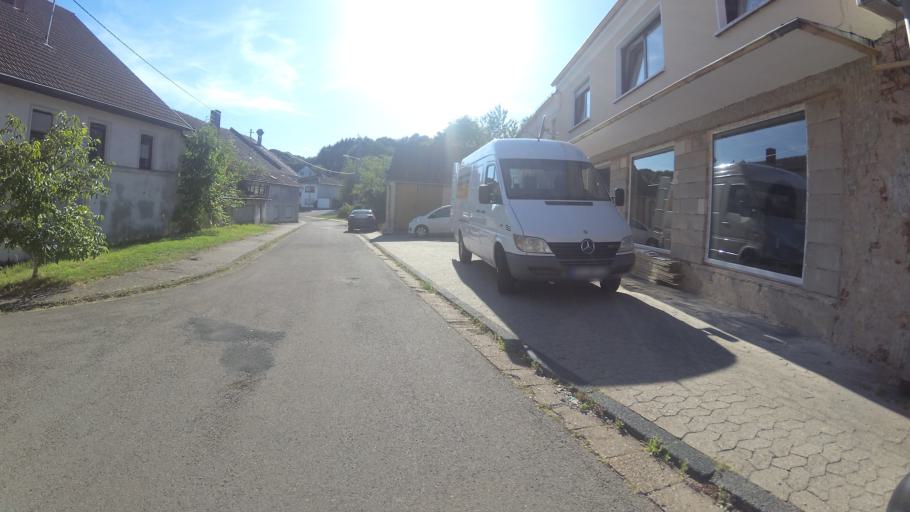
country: DE
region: Saarland
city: Eppelborn
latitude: 49.4739
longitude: 6.9612
